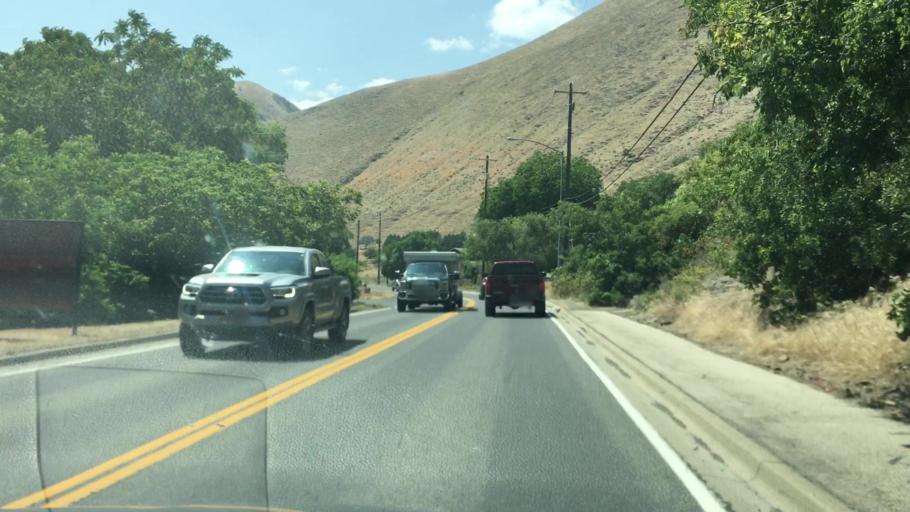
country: US
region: Idaho
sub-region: Idaho County
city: Grangeville
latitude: 45.4140
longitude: -116.3250
